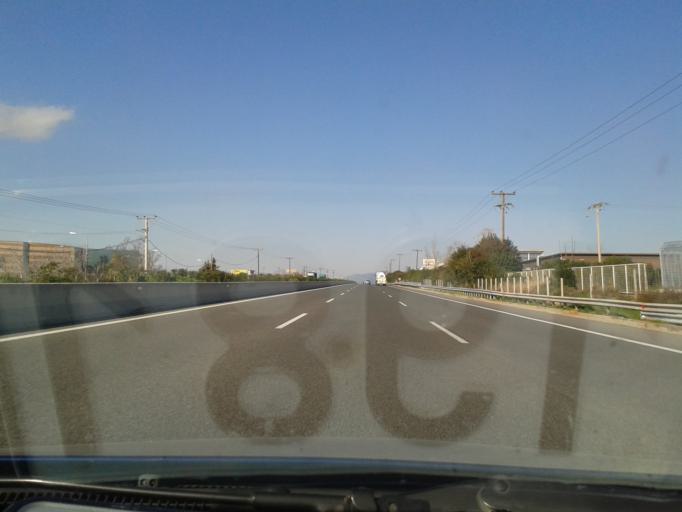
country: GR
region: Central Greece
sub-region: Nomos Voiotias
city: Oinofyta
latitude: 38.3211
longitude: 23.6210
